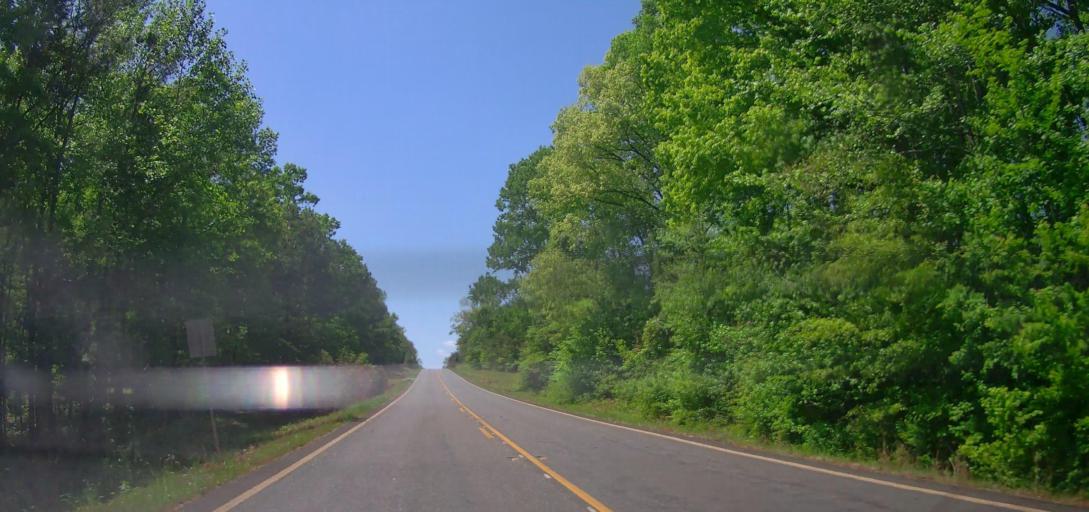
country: US
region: Georgia
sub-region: Jasper County
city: Monticello
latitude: 33.2343
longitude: -83.5355
